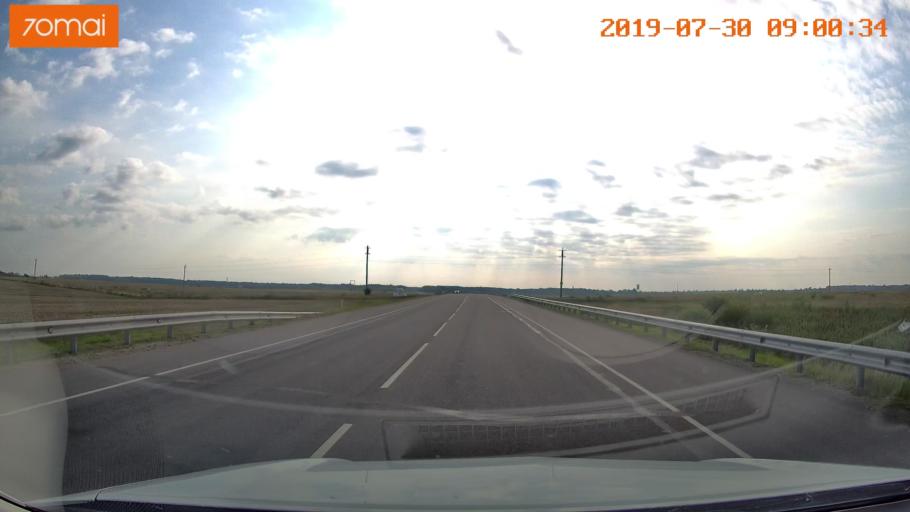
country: RU
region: Kaliningrad
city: Gusev
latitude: 54.6147
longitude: 22.1847
